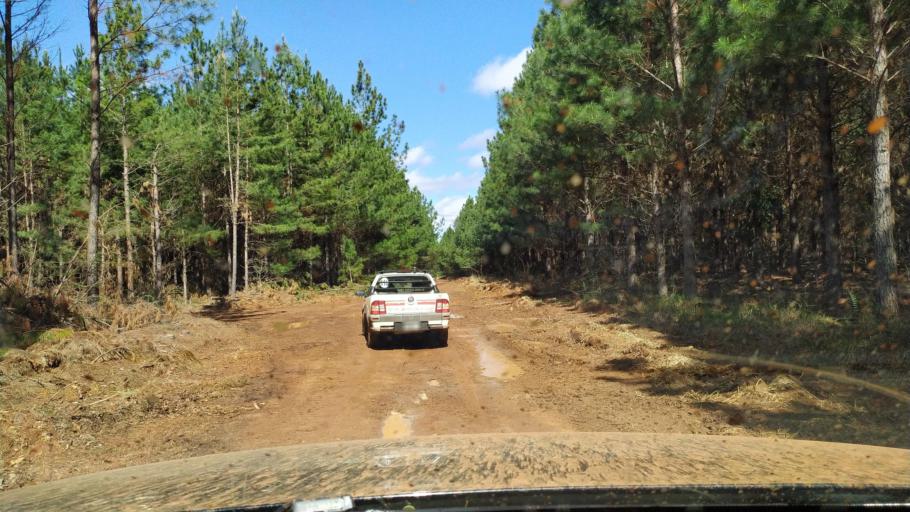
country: AR
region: Corrientes
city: Santo Tome
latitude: -28.4080
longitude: -56.0163
